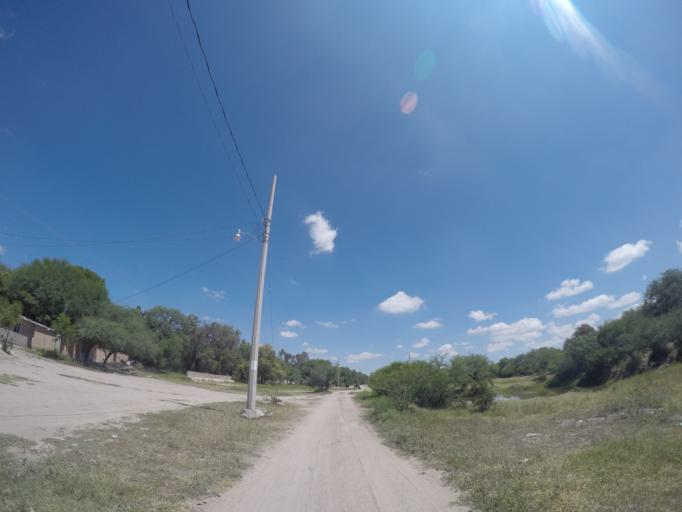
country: MX
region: San Luis Potosi
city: La Pila
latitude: 21.9826
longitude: -100.8982
